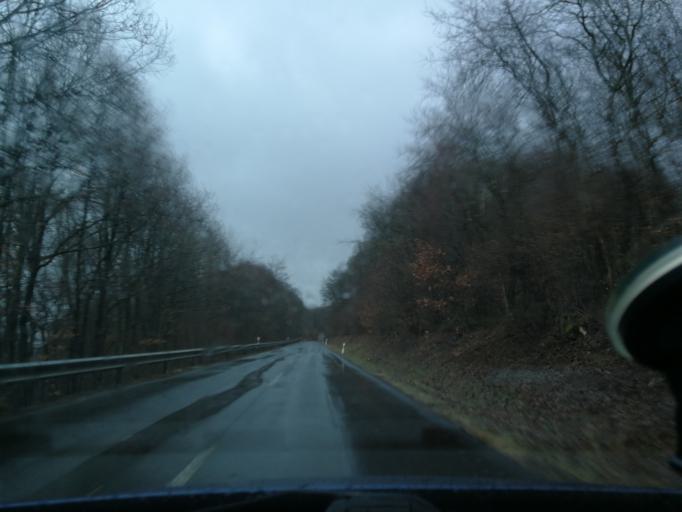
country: DE
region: Rheinland-Pfalz
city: Berglicht
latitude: 49.7807
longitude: 6.9831
